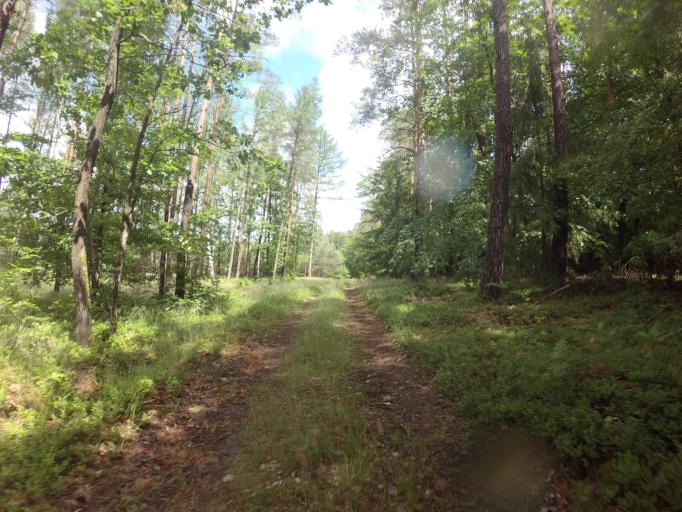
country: PL
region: West Pomeranian Voivodeship
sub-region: Powiat choszczenski
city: Bierzwnik
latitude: 53.0137
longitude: 15.5954
